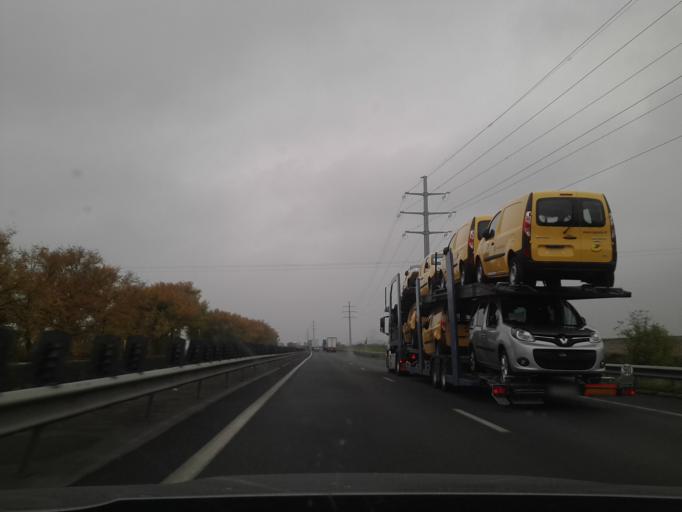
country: FR
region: Nord-Pas-de-Calais
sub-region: Departement du Nord
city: Iwuy
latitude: 50.2434
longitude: 3.3028
